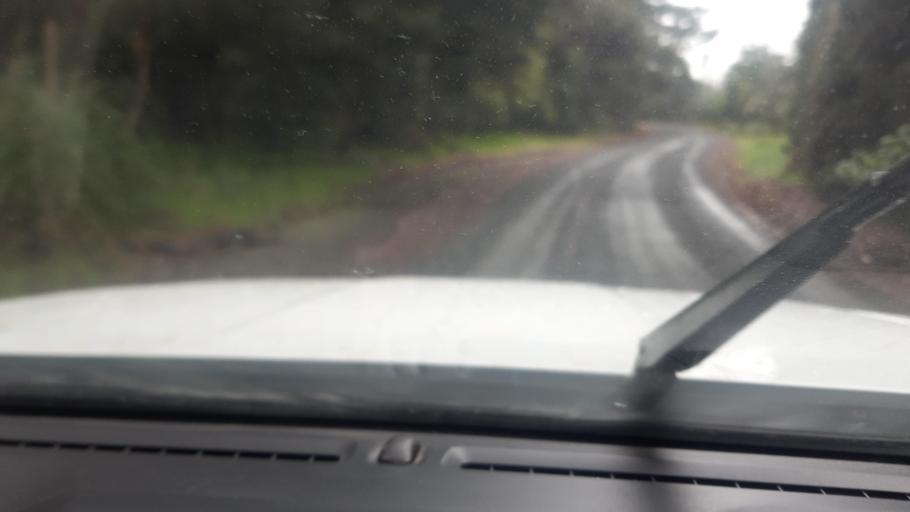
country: NZ
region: Northland
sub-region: Far North District
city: Kaitaia
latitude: -34.9855
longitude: 173.2086
